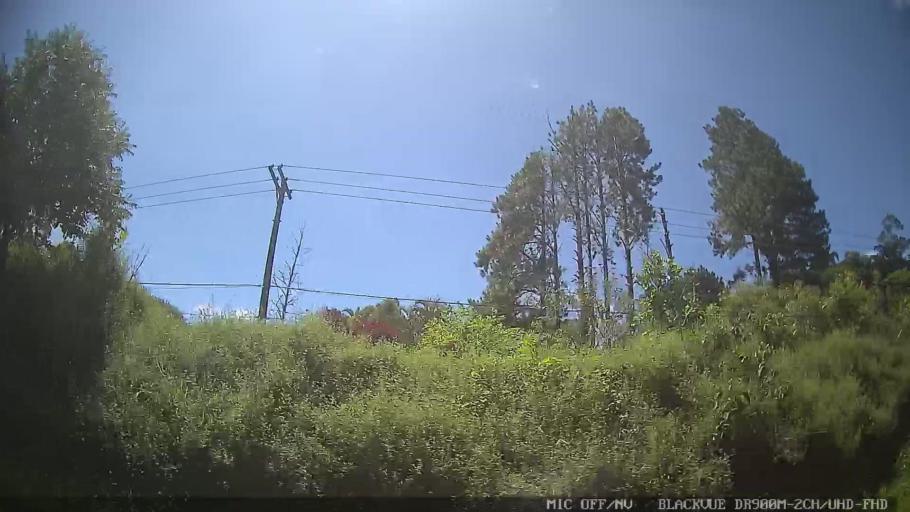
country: BR
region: Sao Paulo
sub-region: Mogi das Cruzes
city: Mogi das Cruzes
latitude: -23.6099
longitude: -46.1731
